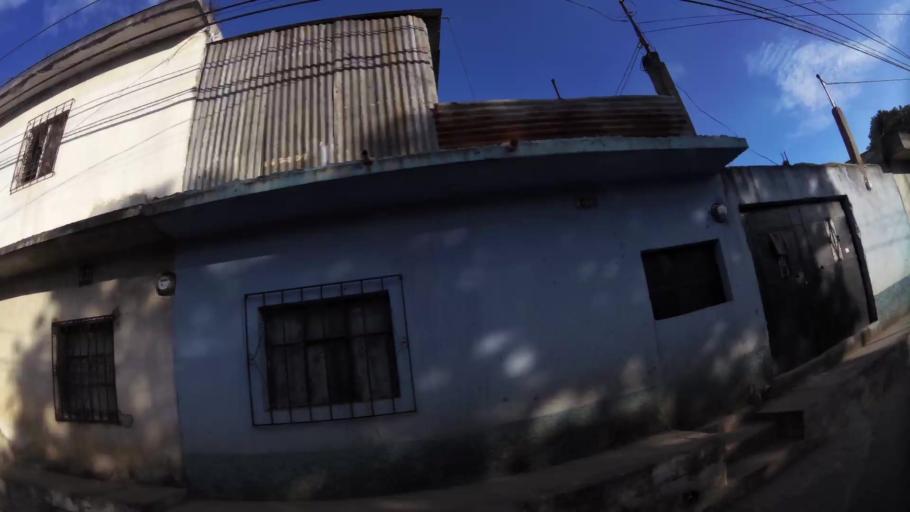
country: GT
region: Guatemala
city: Villa Nueva
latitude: 14.5206
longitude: -90.5789
